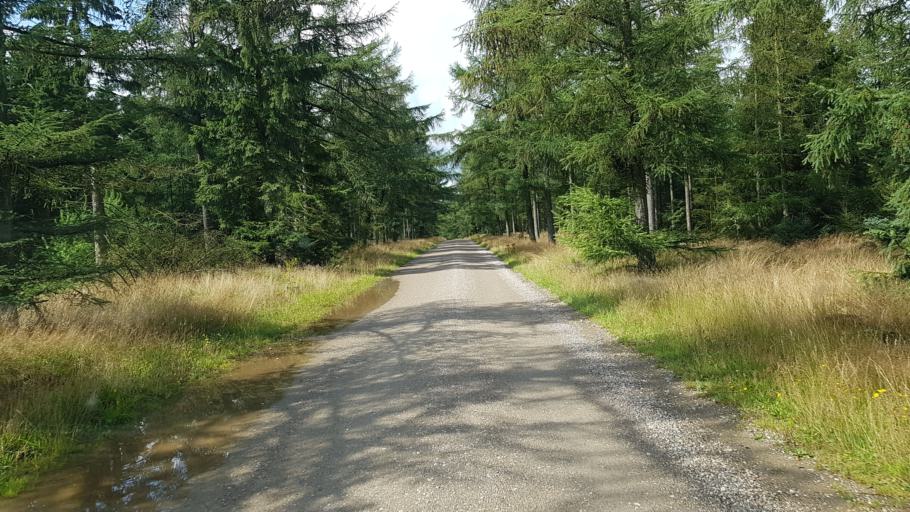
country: DK
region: South Denmark
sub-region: Vejen Kommune
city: Holsted
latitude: 55.5949
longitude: 8.9066
